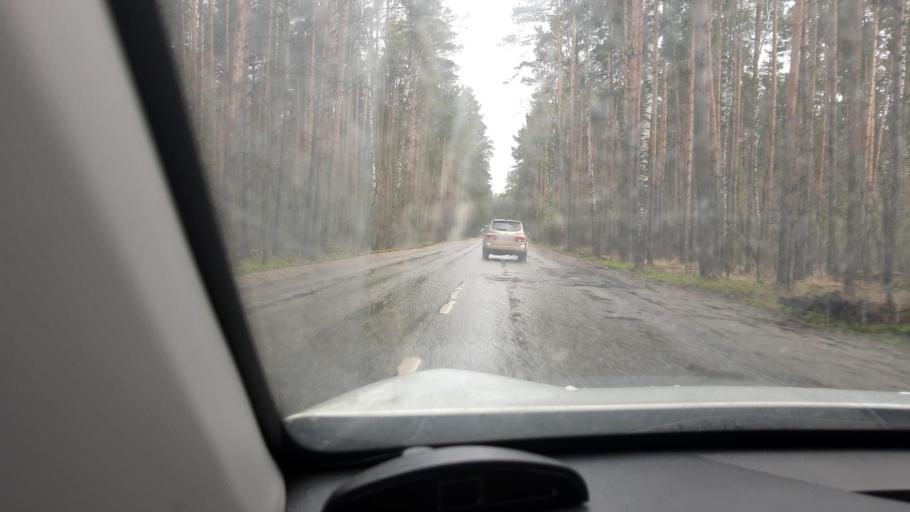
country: RU
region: Moskovskaya
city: Rodniki
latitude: 55.6758
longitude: 38.1063
